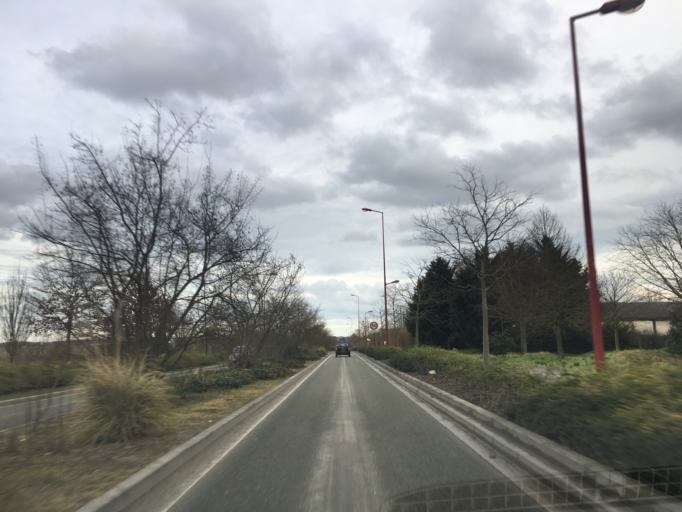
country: FR
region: Ile-de-France
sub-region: Departement du Val-d'Oise
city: Arnouville
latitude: 49.0012
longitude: 2.4306
